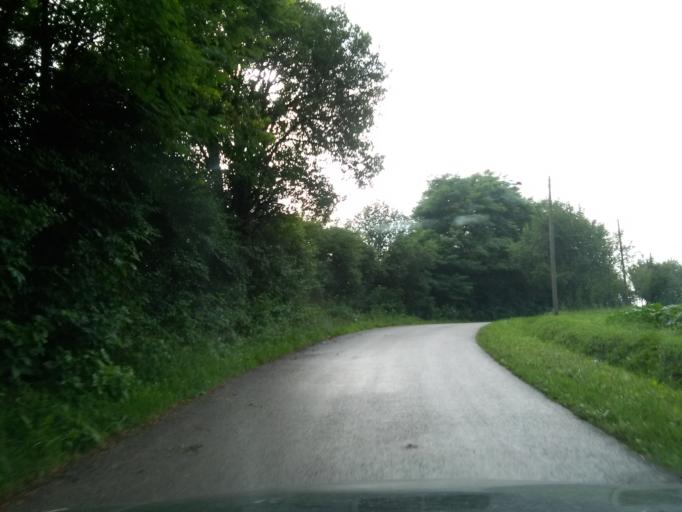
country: HR
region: Sisacko-Moslavacka
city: Gvozd
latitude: 45.2767
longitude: 15.9641
